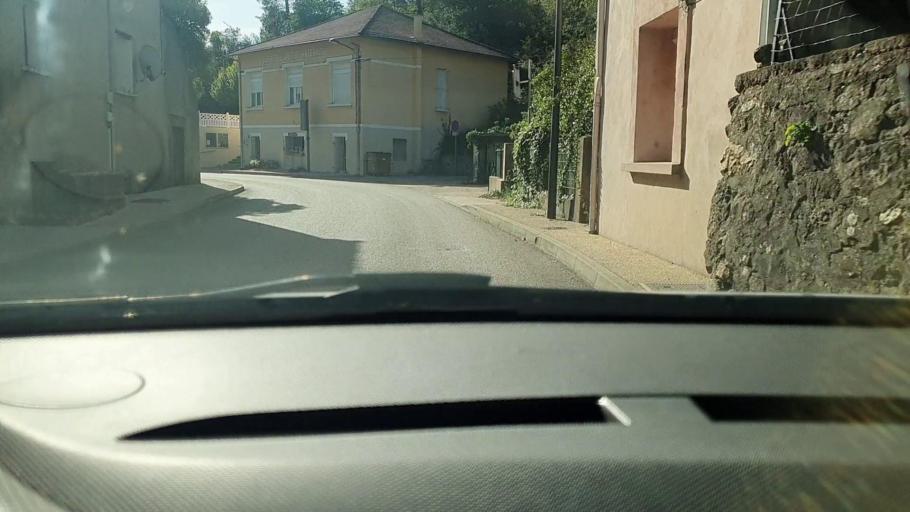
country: FR
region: Languedoc-Roussillon
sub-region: Departement du Gard
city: Saint-Florent-sur-Auzonnet
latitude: 44.2532
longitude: 4.0845
